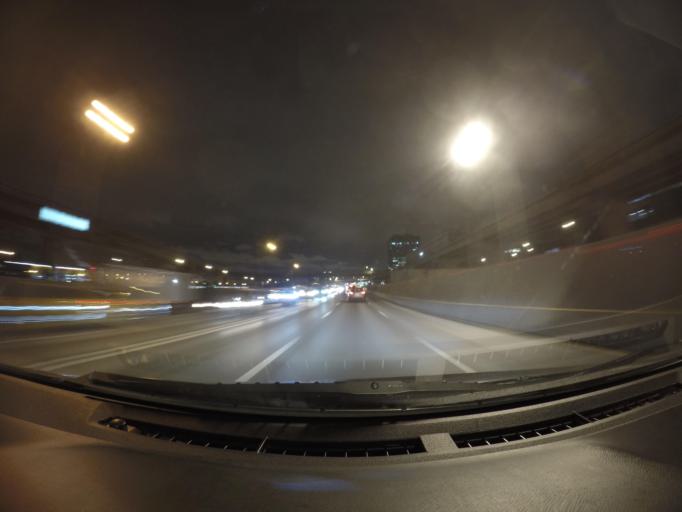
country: RU
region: Moscow
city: Tekstil'shchiki
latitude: 55.7113
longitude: 37.7241
